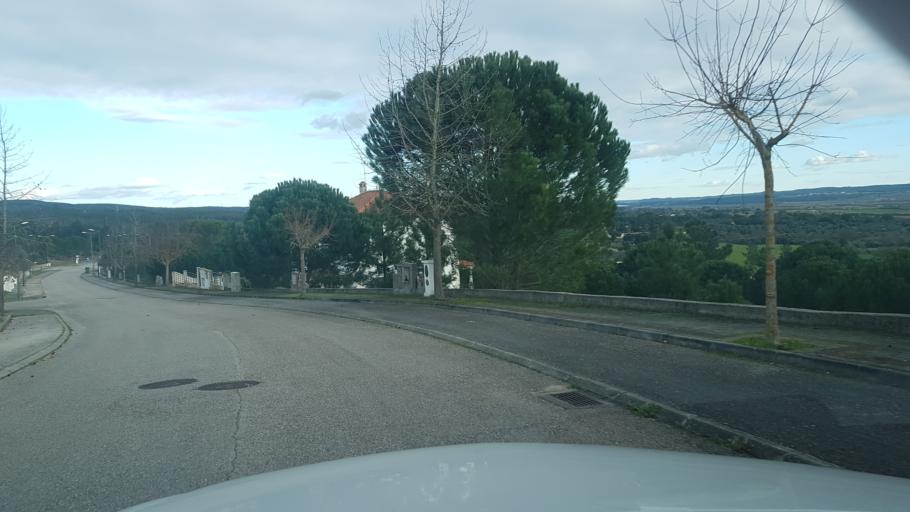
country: PT
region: Santarem
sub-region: Constancia
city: Constancia
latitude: 39.4821
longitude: -8.3305
